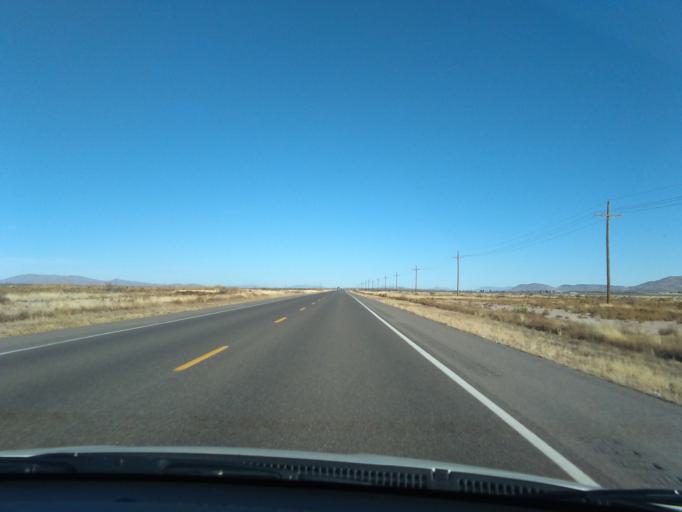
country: US
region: New Mexico
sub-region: Dona Ana County
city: Hatch
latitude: 32.5950
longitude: -107.3433
